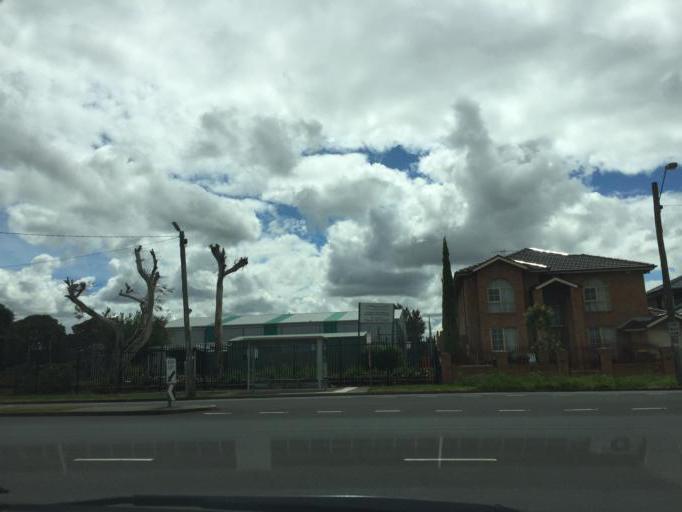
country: AU
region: Victoria
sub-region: Maribyrnong
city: Braybrook
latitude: -37.7921
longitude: 144.8548
